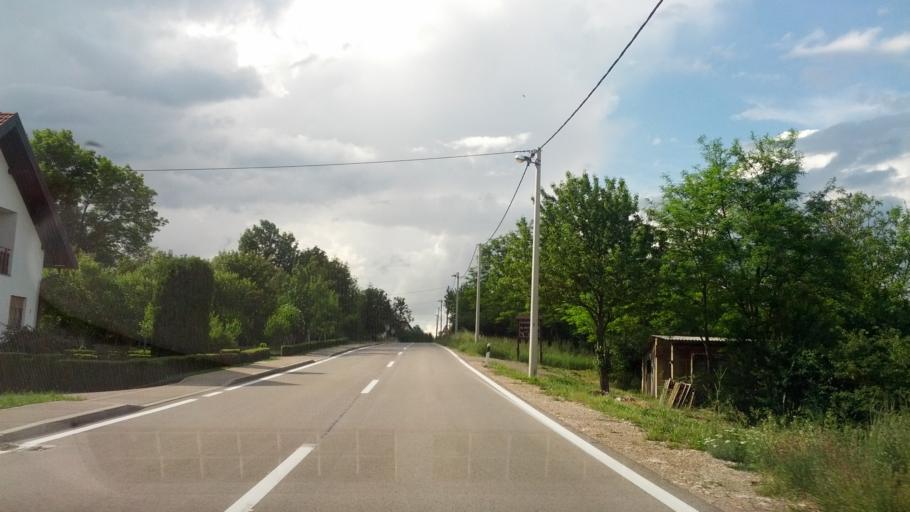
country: BA
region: Federation of Bosnia and Herzegovina
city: Izacic
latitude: 44.9041
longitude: 15.7228
